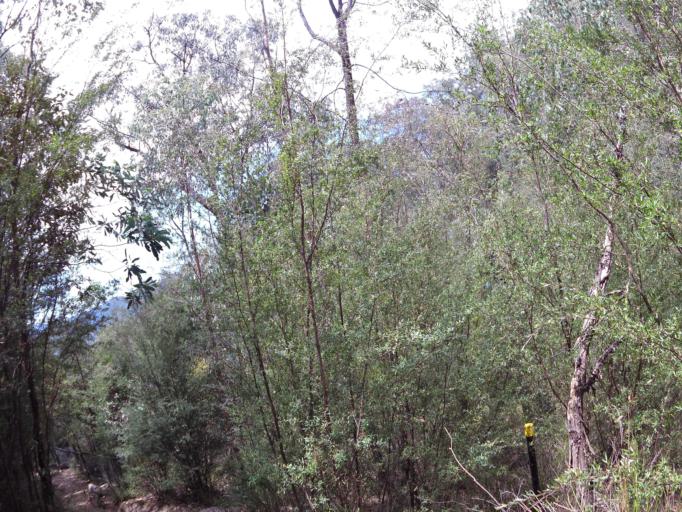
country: AU
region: Victoria
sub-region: Alpine
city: Mount Beauty
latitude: -36.7186
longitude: 146.8375
